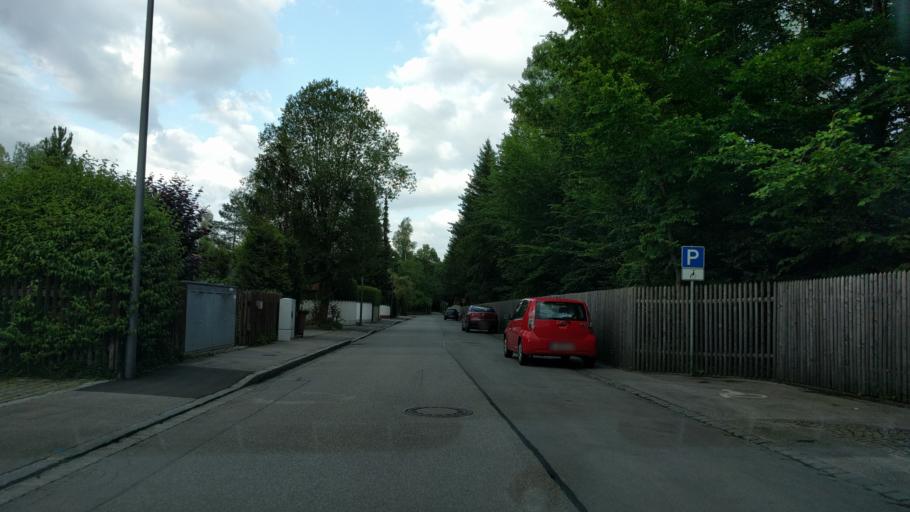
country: DE
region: Bavaria
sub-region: Upper Bavaria
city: Grunwald
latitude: 48.0313
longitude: 11.5222
